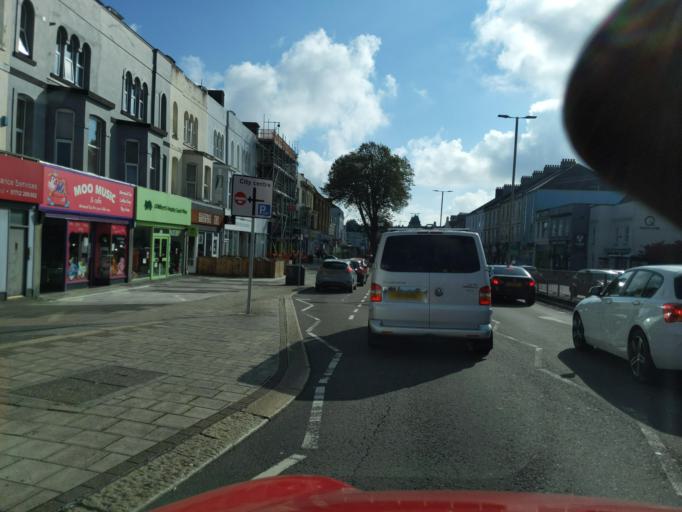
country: GB
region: England
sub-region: Plymouth
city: Plymouth
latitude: 50.3838
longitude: -4.1344
